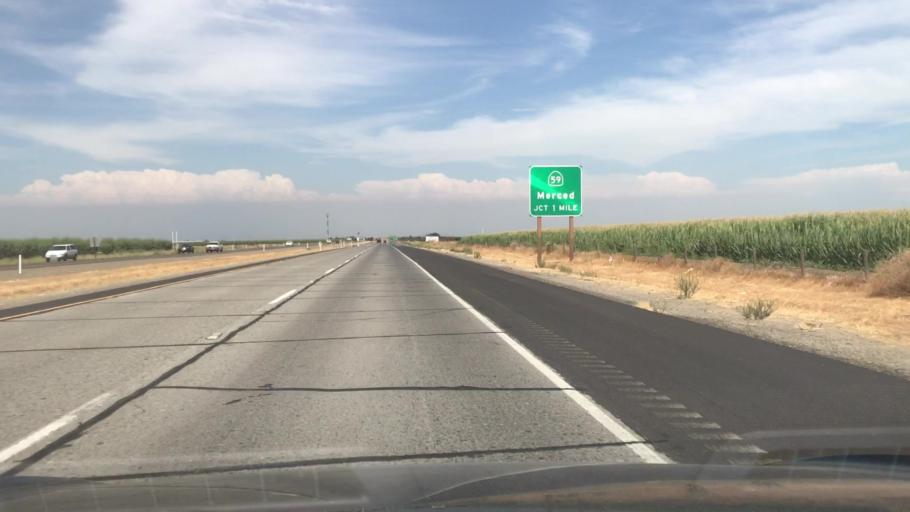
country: US
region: California
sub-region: Merced County
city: Dos Palos
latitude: 37.0755
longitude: -120.5125
